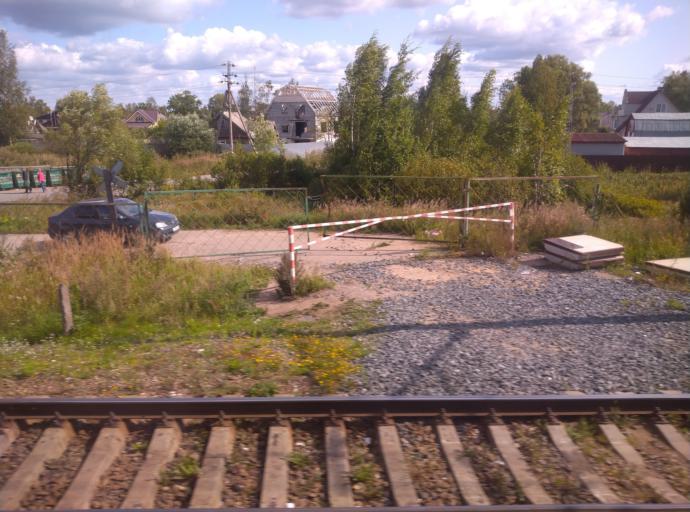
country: RU
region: Leningrad
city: Ul'yanovka
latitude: 59.6331
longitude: 30.7607
